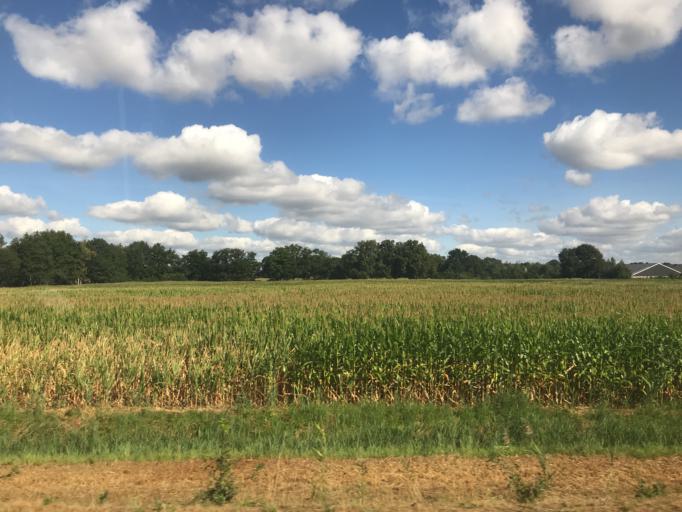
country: NL
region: Gelderland
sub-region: Gemeente Lochem
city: Laren
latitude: 52.2744
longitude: 6.3658
